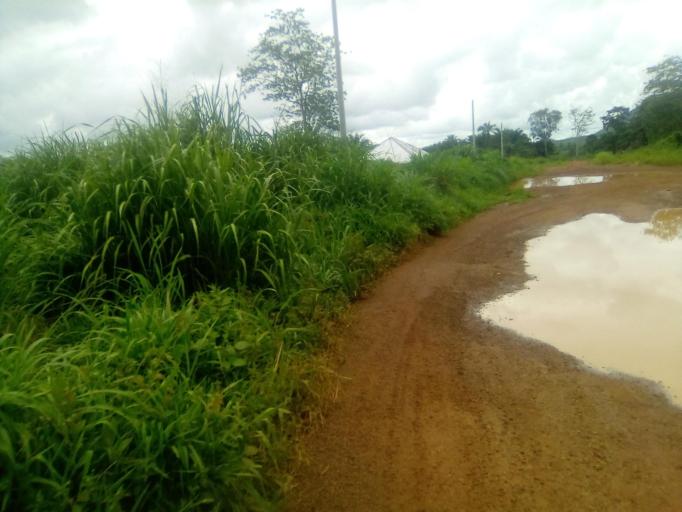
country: SL
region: Southern Province
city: Moyamba
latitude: 8.1421
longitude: -12.4404
